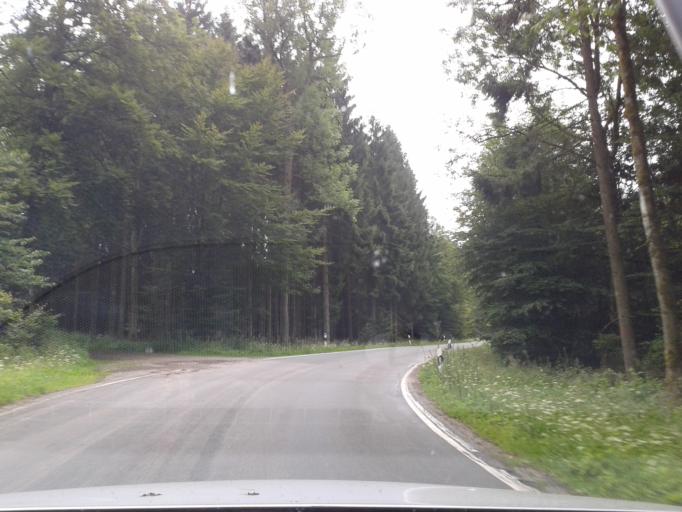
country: DE
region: North Rhine-Westphalia
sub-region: Regierungsbezirk Detmold
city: Barntrup
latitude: 51.9529
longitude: 9.1383
